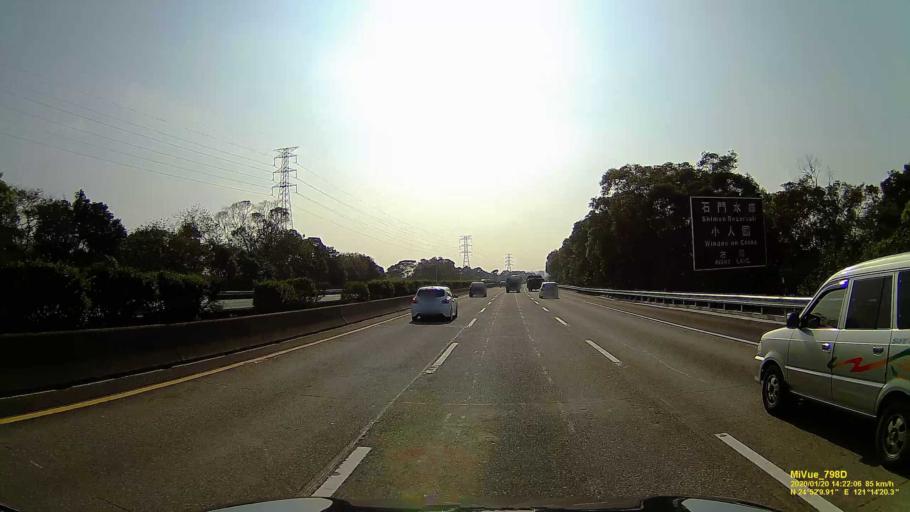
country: TW
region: Taiwan
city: Daxi
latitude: 24.8688
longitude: 121.2390
